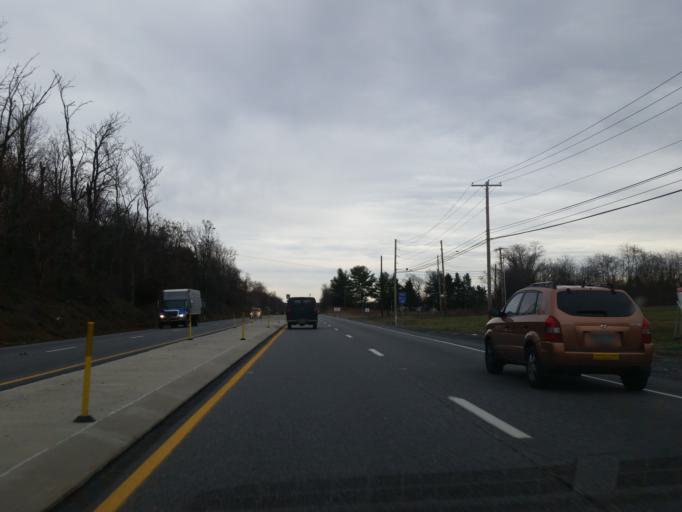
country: US
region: Pennsylvania
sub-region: Dauphin County
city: Skyline View
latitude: 40.3399
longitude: -76.7090
